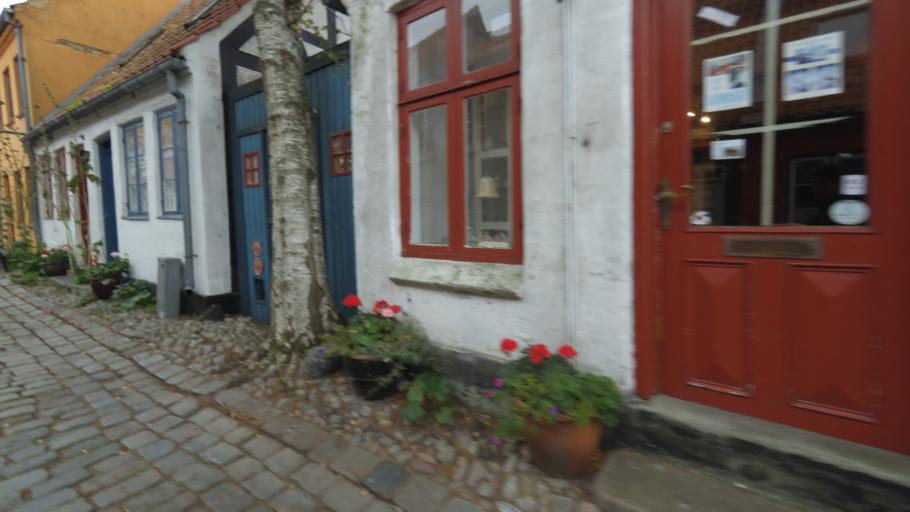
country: DK
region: Central Jutland
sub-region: Arhus Kommune
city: Arhus
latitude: 56.1568
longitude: 10.2025
